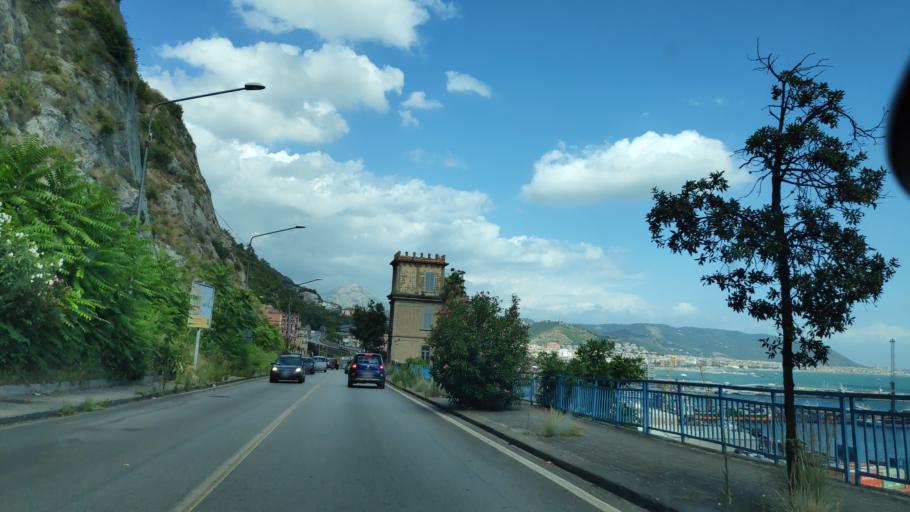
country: IT
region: Campania
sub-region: Provincia di Salerno
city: Vietri sul Mare
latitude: 40.6769
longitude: 14.7394
